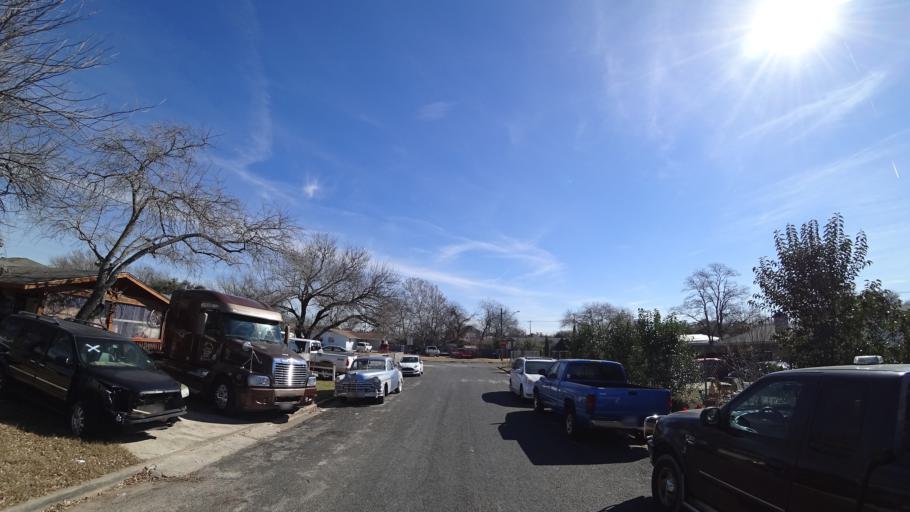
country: US
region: Texas
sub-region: Travis County
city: Wells Branch
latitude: 30.3834
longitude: -97.6963
